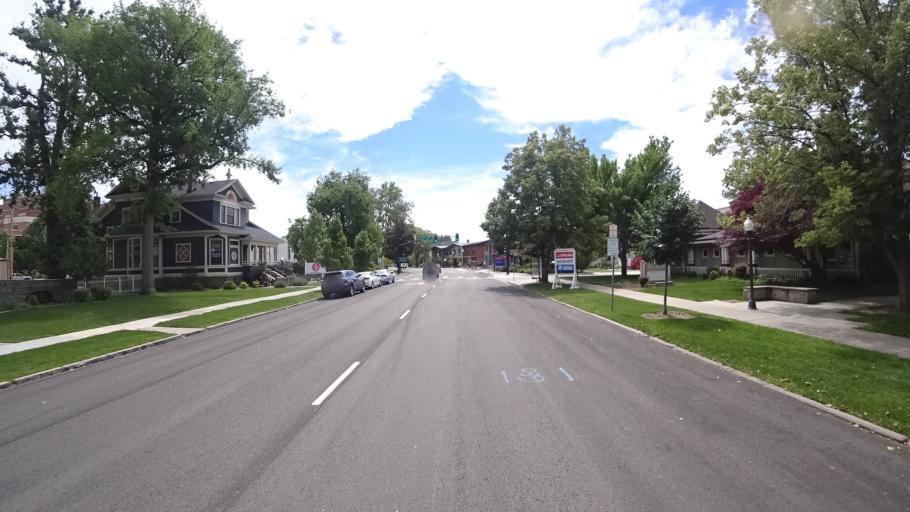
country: US
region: Idaho
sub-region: Ada County
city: Boise
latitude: 43.6118
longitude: -116.1959
